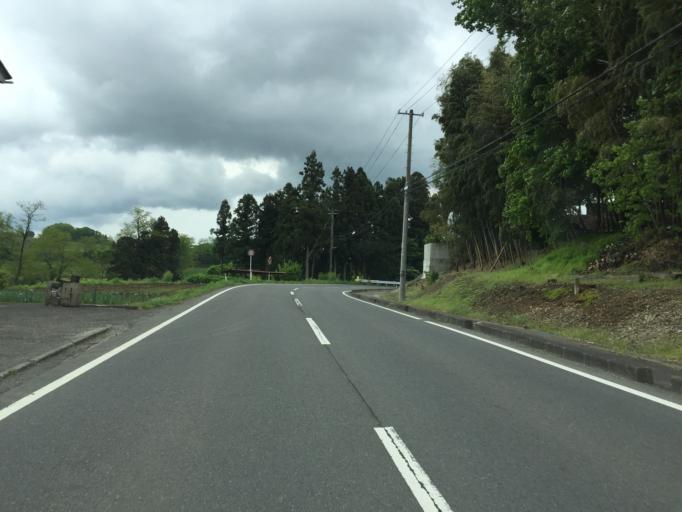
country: JP
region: Fukushima
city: Ishikawa
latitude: 37.1783
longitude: 140.4075
